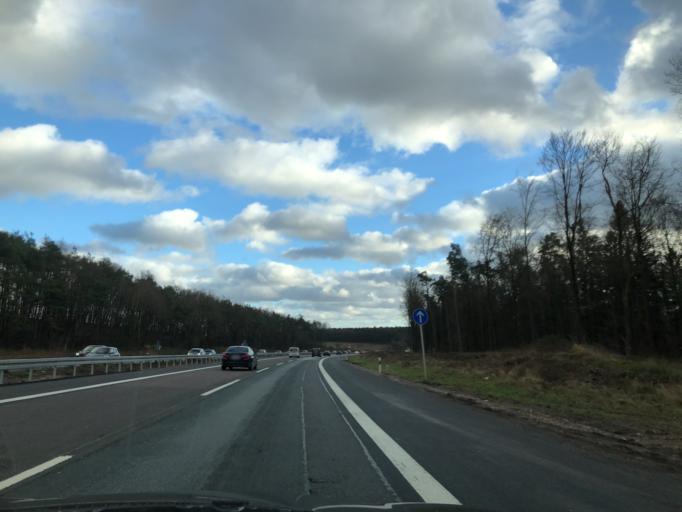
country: DE
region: Bavaria
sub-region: Regierungsbezirk Unterfranken
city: Bischbrunn
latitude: 49.8546
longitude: 9.4956
